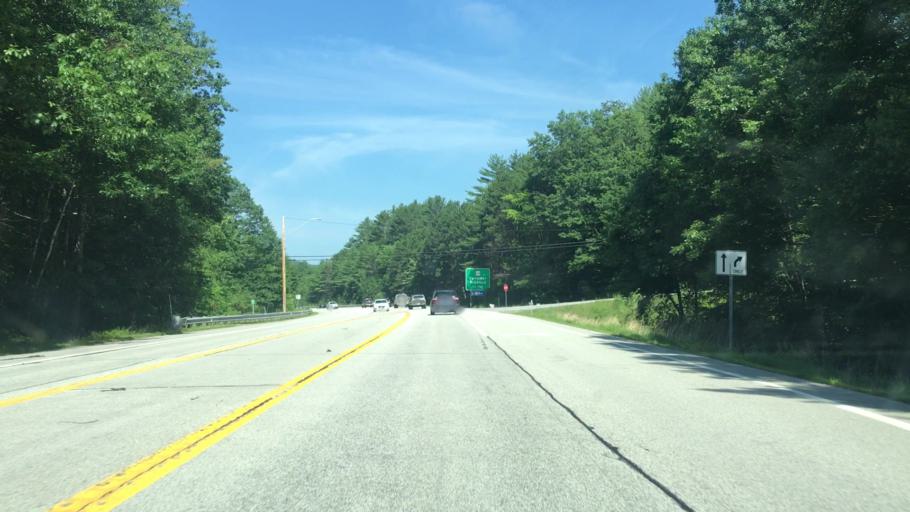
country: US
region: New Hampshire
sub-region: Merrimack County
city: Henniker
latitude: 43.1895
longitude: -71.8102
